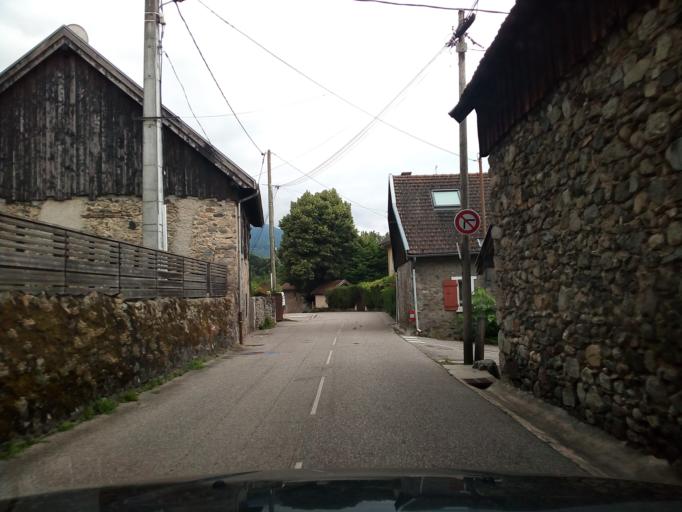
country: FR
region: Rhone-Alpes
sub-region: Departement de l'Isere
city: Vaulnaveys-le-Haut
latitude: 45.1350
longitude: 5.8362
